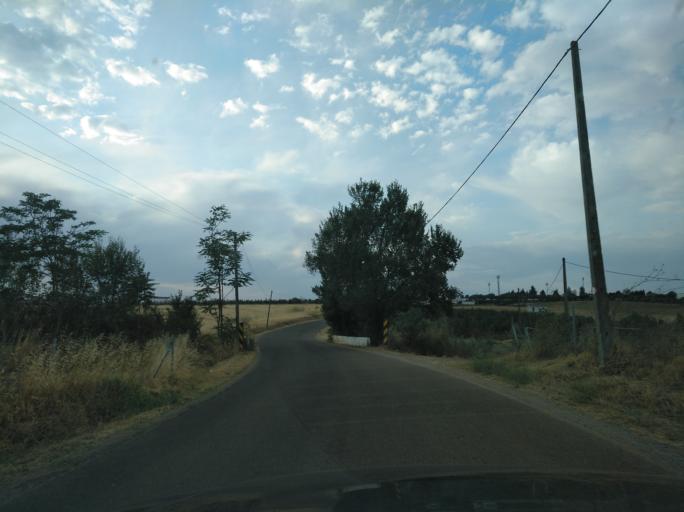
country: PT
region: Portalegre
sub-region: Campo Maior
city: Campo Maior
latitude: 39.0060
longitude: -7.0607
